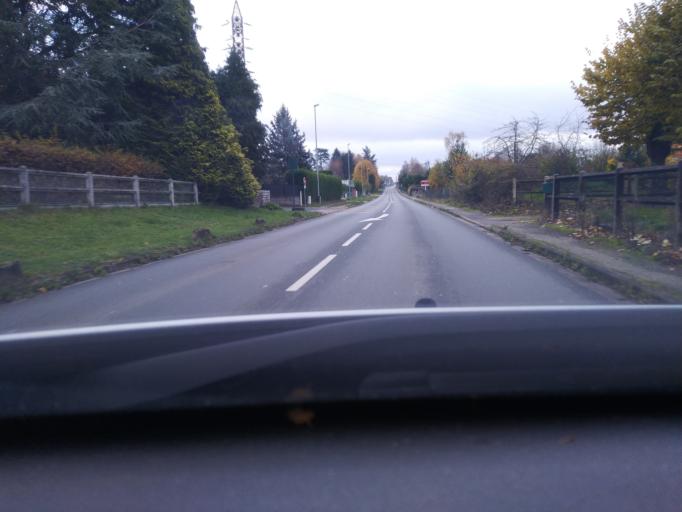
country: FR
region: Haute-Normandie
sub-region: Departement de la Seine-Maritime
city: La Vaupaliere
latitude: 49.4888
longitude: 1.0039
